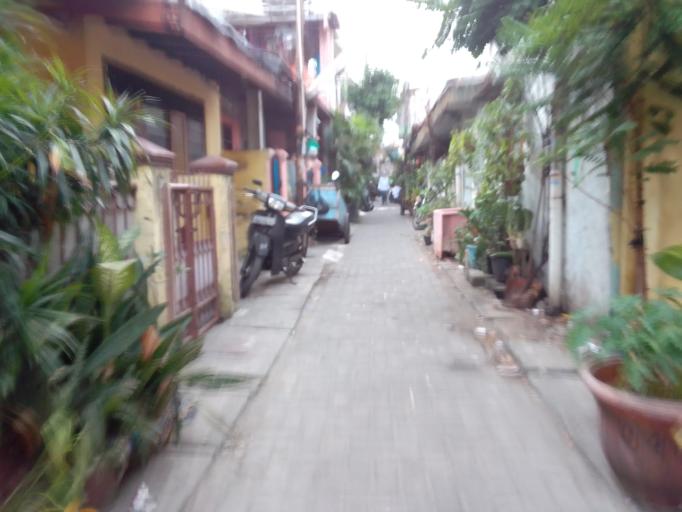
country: ID
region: Jakarta Raya
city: Jakarta
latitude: -6.1652
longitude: 106.8053
